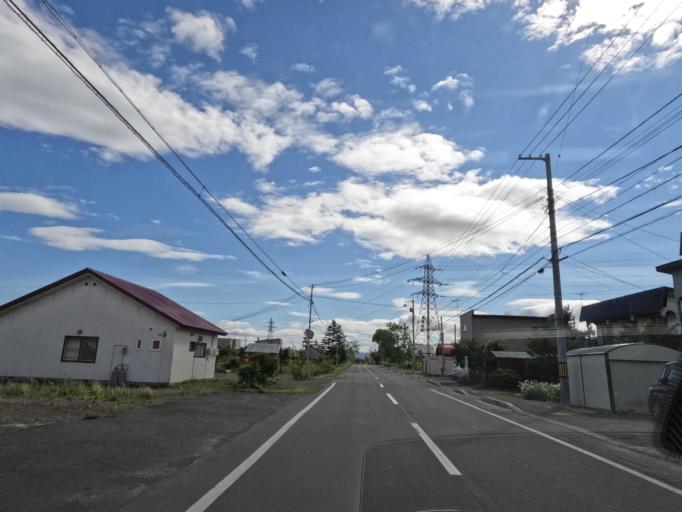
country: JP
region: Hokkaido
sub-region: Asahikawa-shi
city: Asahikawa
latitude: 43.8250
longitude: 142.5205
